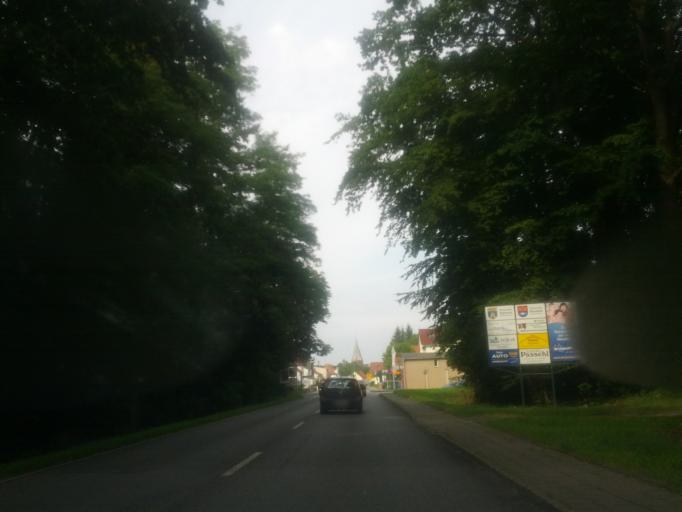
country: DE
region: Mecklenburg-Vorpommern
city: Neubukow
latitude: 54.0259
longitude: 11.6635
